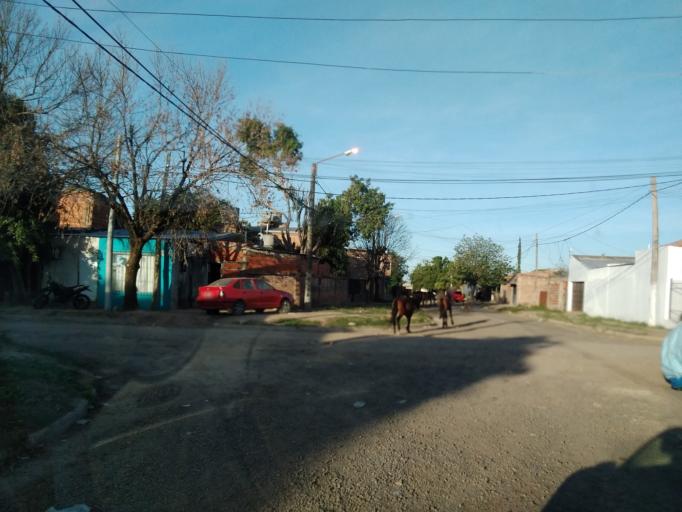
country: AR
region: Corrientes
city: Corrientes
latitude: -27.4998
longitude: -58.8322
